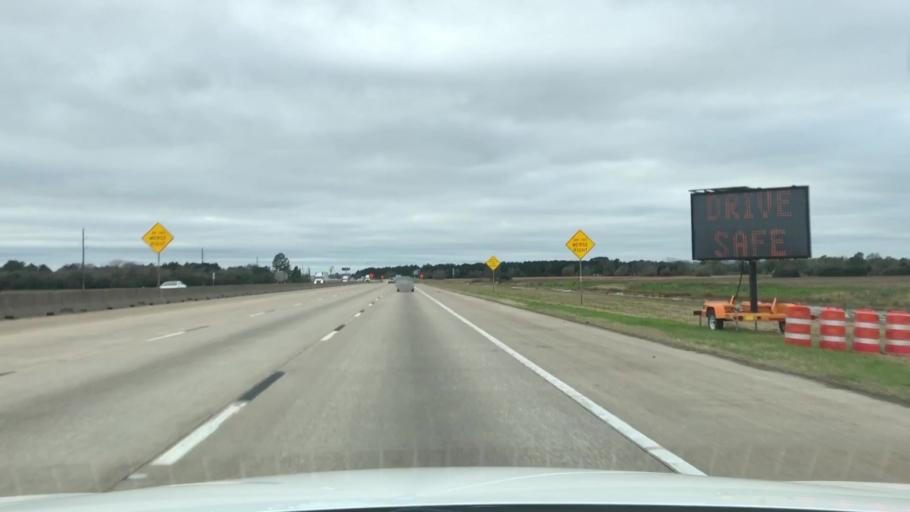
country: US
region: Texas
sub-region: Waller County
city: Brookshire
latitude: 29.7783
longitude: -95.9312
